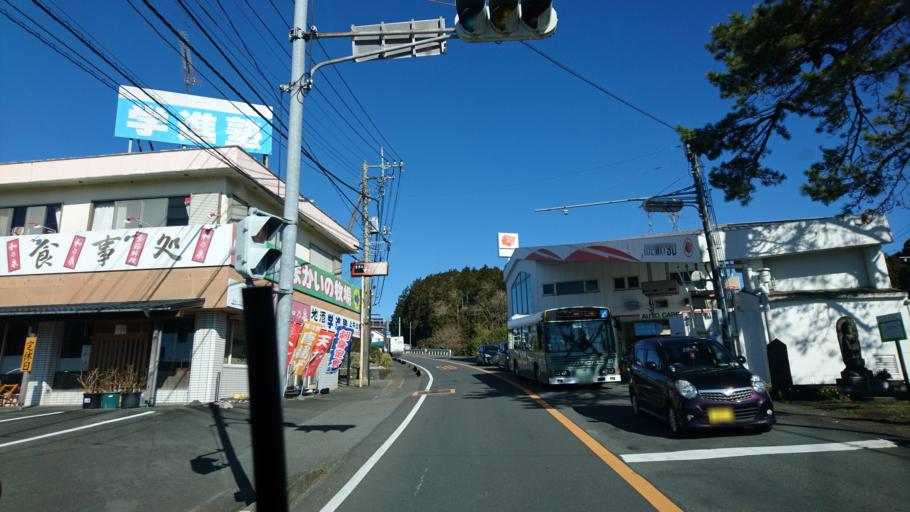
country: JP
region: Shizuoka
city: Fujinomiya
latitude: 35.3126
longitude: 138.5931
